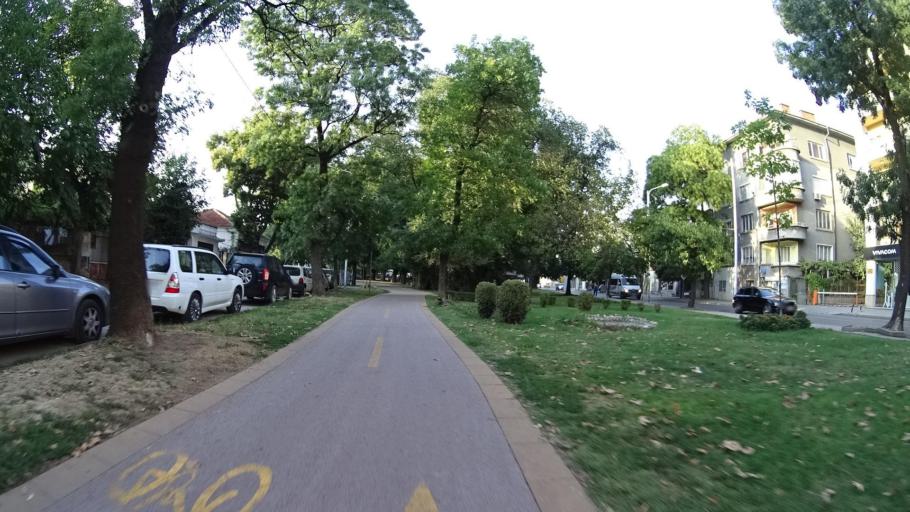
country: BG
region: Plovdiv
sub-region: Obshtina Plovdiv
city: Plovdiv
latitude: 42.1290
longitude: 24.7432
